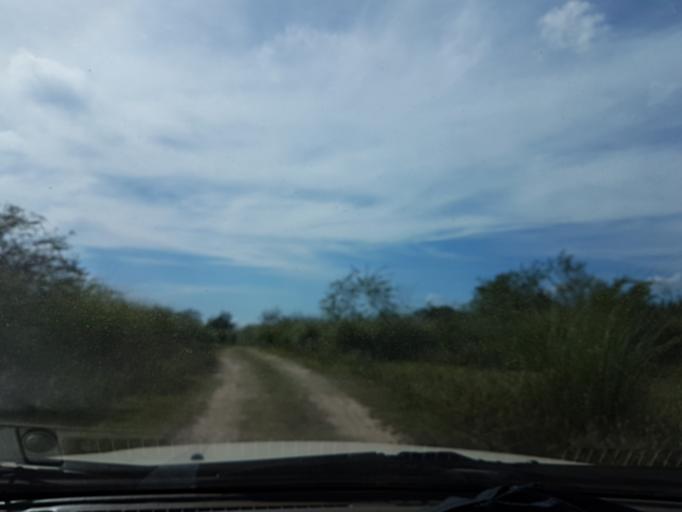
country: PY
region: Cordillera
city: Arroyos y Esteros
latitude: -24.9709
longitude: -57.1929
